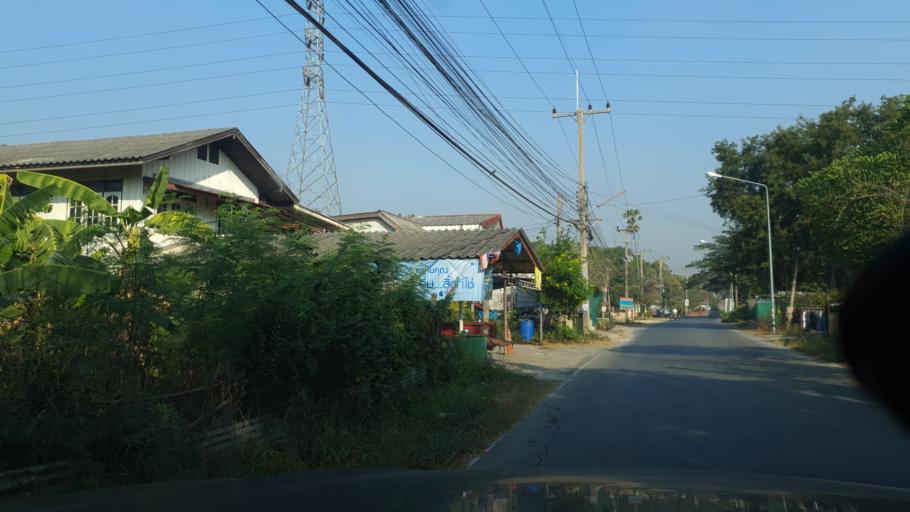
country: TH
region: Phra Nakhon Si Ayutthaya
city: Phra Nakhon Si Ayutthaya
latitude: 14.3672
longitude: 100.5597
